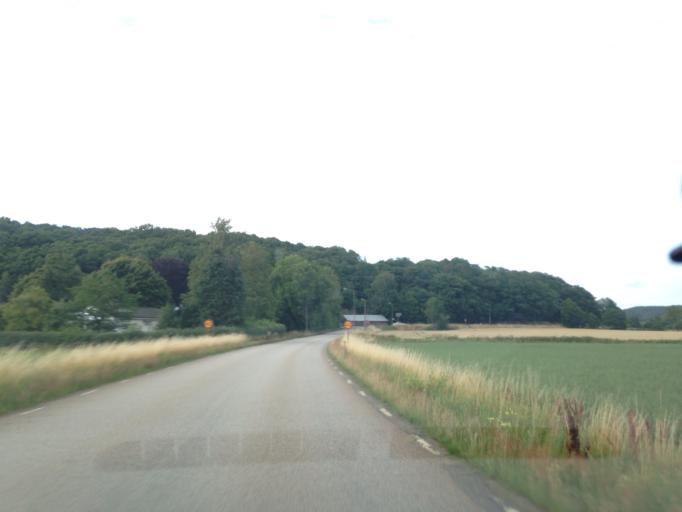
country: SE
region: Halland
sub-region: Varbergs Kommun
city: Tvaaker
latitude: 57.1415
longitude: 12.4644
